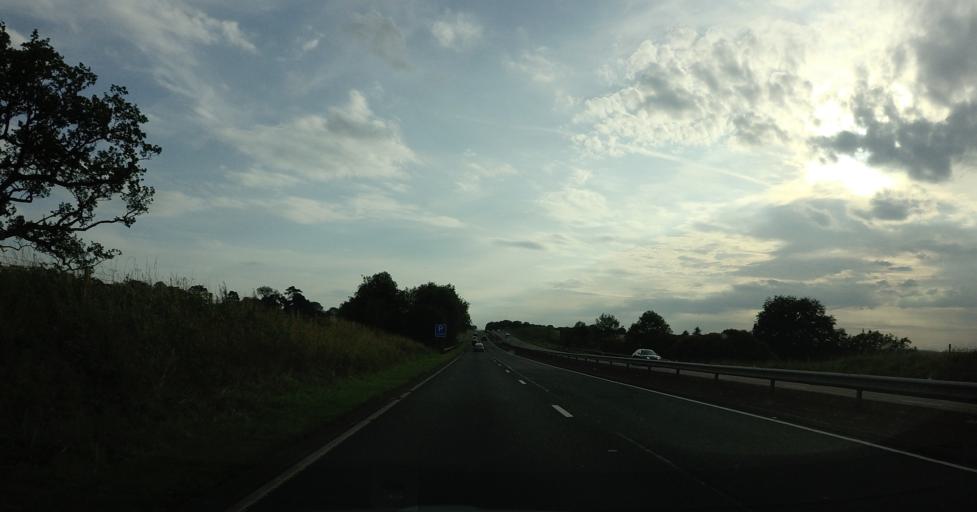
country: GB
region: Scotland
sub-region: Stirling
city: Dunblane
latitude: 56.2348
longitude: -3.8995
